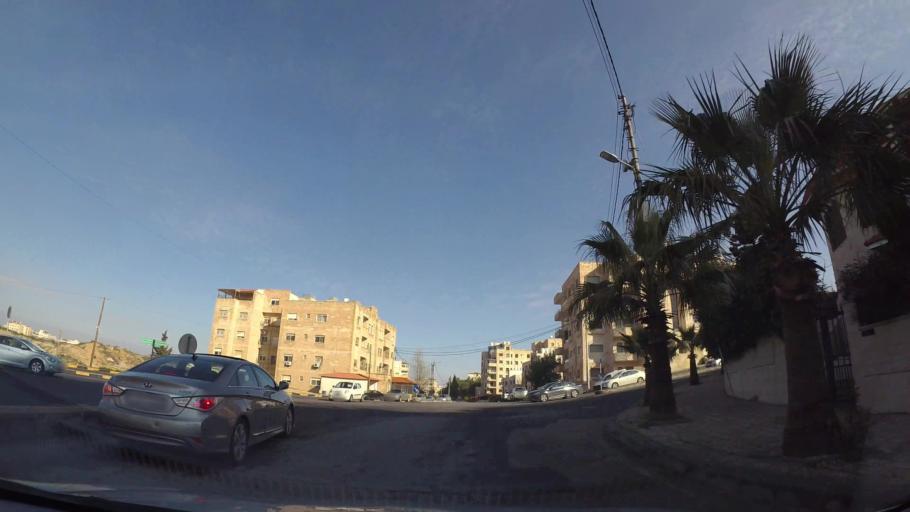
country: JO
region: Amman
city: Al Jubayhah
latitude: 32.0059
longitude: 35.8509
